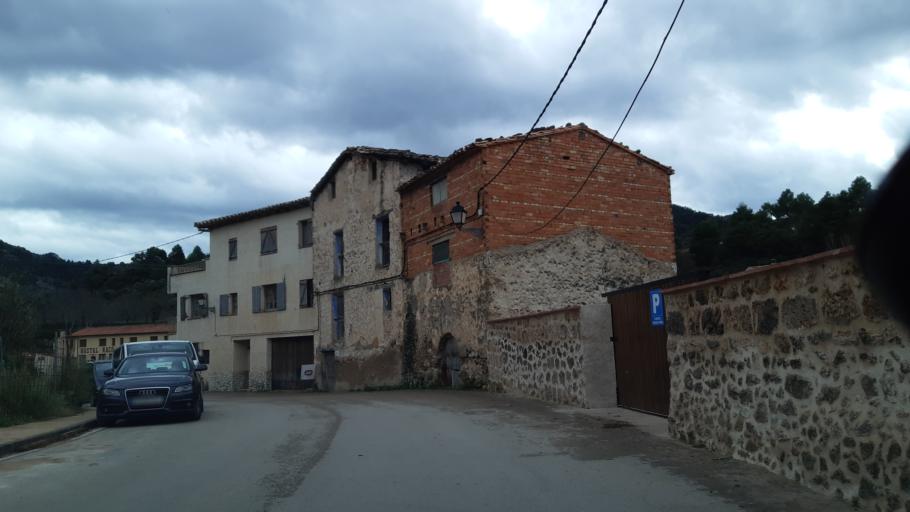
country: ES
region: Aragon
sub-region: Provincia de Teruel
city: Valderrobres
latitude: 40.8308
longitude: 0.1815
